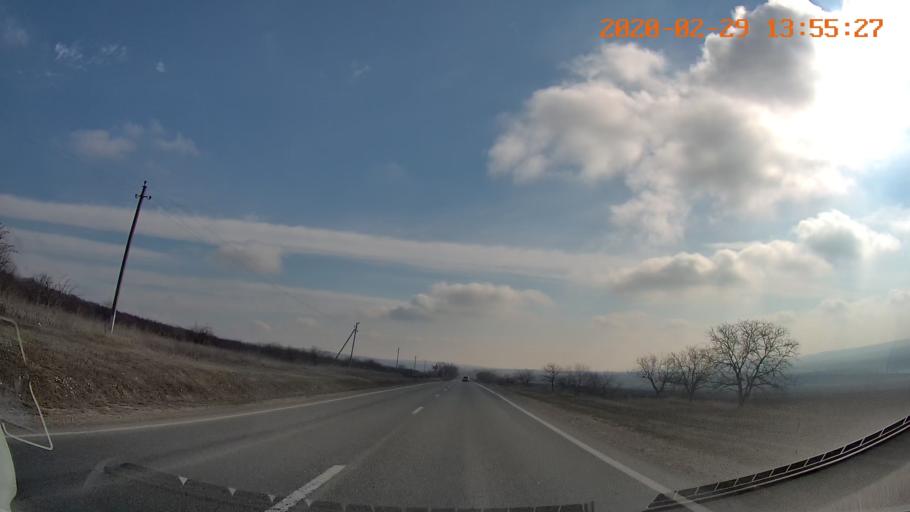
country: MD
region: Floresti
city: Leninskiy
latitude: 47.8188
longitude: 28.4363
